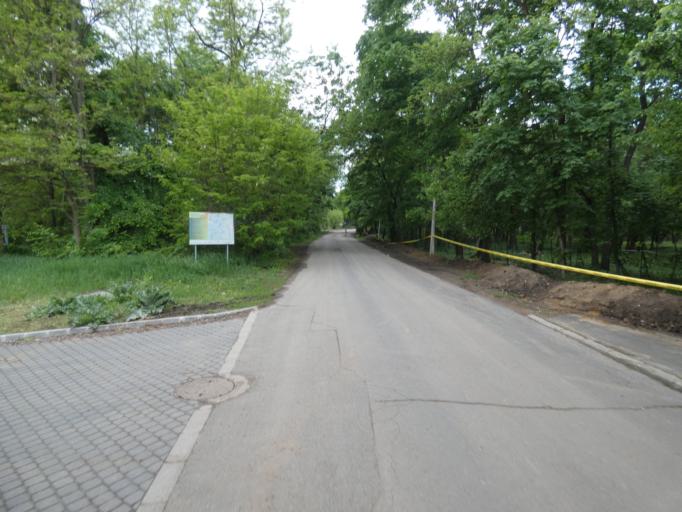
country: HU
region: Szabolcs-Szatmar-Bereg
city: Kotaj
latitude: 48.0065
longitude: 21.7212
